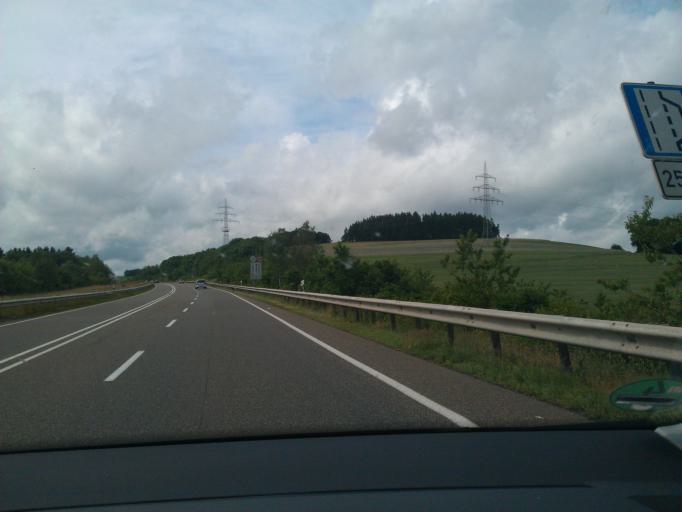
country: DE
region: Rheinland-Pfalz
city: Watzerath
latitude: 50.1933
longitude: 6.3794
